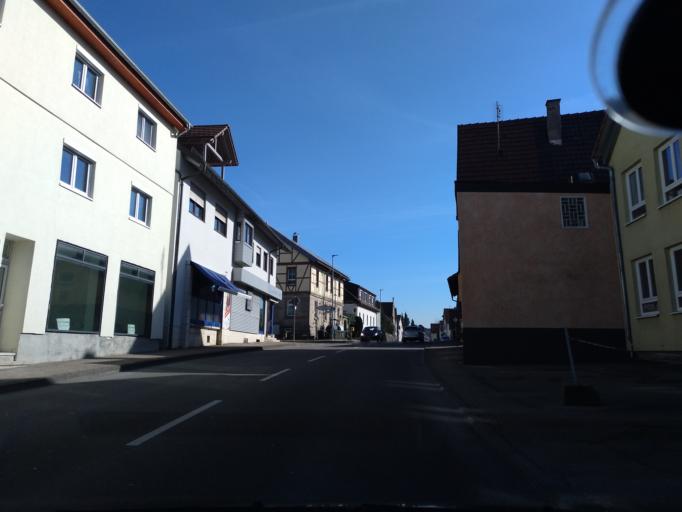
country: DE
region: Baden-Wuerttemberg
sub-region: Regierungsbezirk Stuttgart
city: Bretzfeld
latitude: 49.1653
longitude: 9.4475
